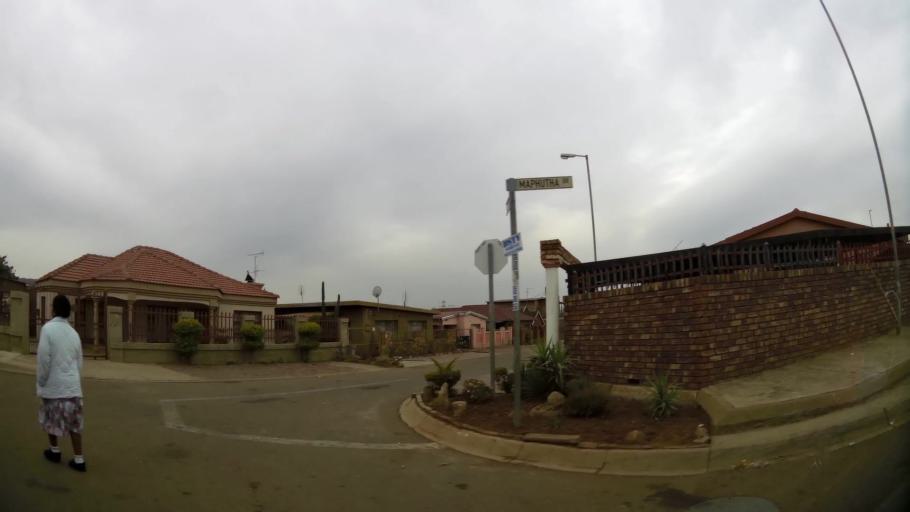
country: ZA
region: Gauteng
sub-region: City of Tshwane Metropolitan Municipality
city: Cullinan
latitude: -25.7119
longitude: 28.3649
